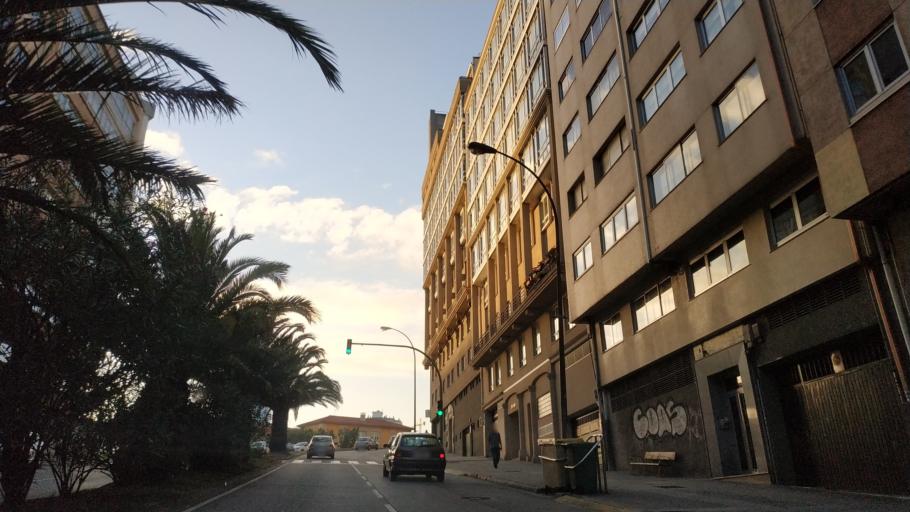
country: ES
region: Galicia
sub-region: Provincia da Coruna
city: A Coruna
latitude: 43.3584
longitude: -8.4089
